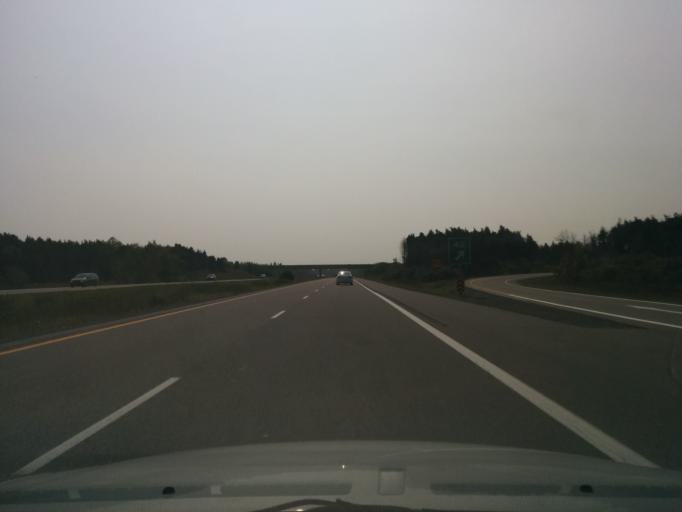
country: CA
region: Ontario
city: Bells Corners
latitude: 45.0964
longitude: -75.6552
